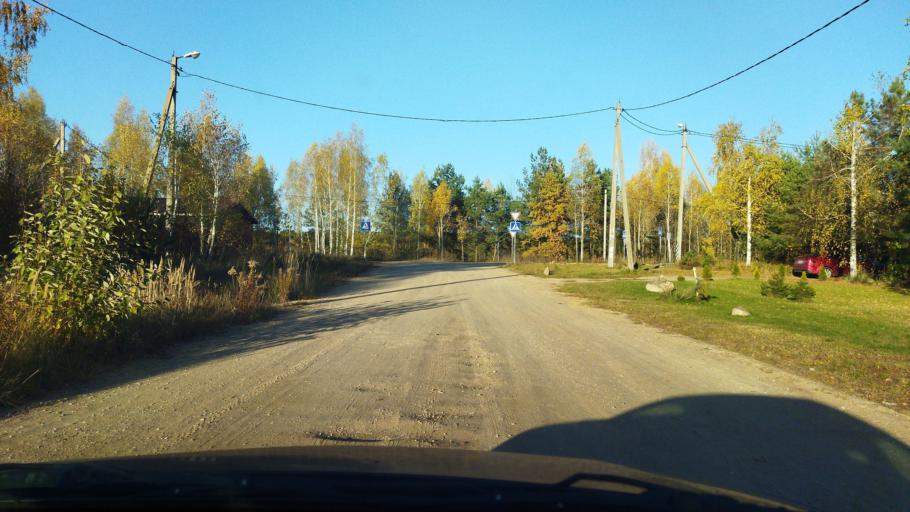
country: BY
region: Minsk
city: Kalodzishchy
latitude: 53.9140
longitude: 27.7721
